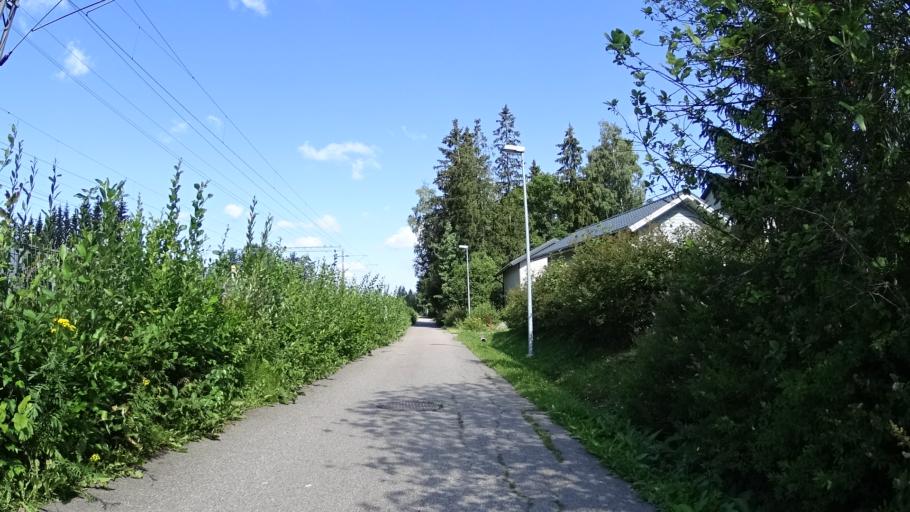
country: FI
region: Uusimaa
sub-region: Helsinki
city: Jaervenpaeae
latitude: 60.4681
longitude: 25.0981
